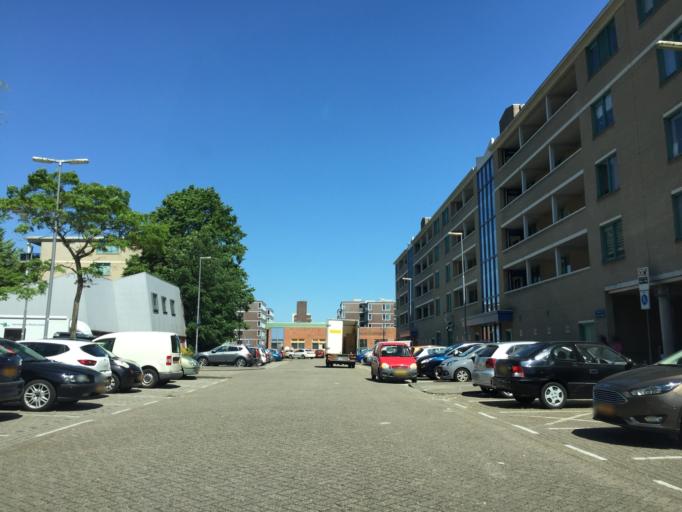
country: NL
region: South Holland
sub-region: Gemeente Rotterdam
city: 's-Gravenland
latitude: 51.9405
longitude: 4.5474
